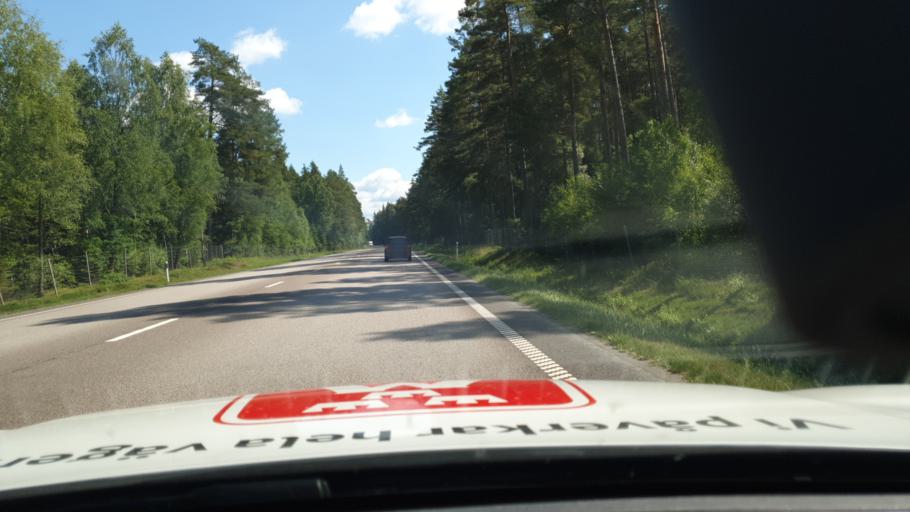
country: SE
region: Vaestra Goetaland
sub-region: Lidkopings Kommun
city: Vinninga
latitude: 58.4723
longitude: 13.2097
